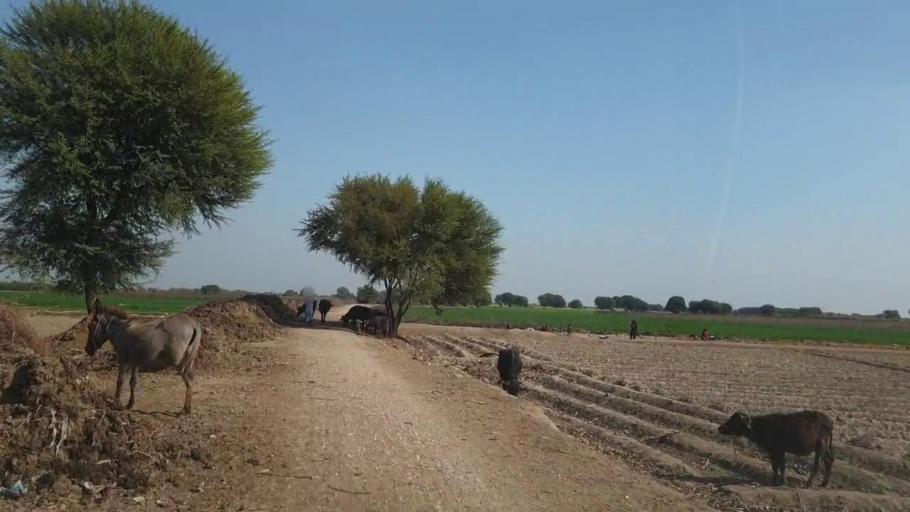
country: PK
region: Sindh
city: Tando Jam
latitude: 25.5043
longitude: 68.4972
